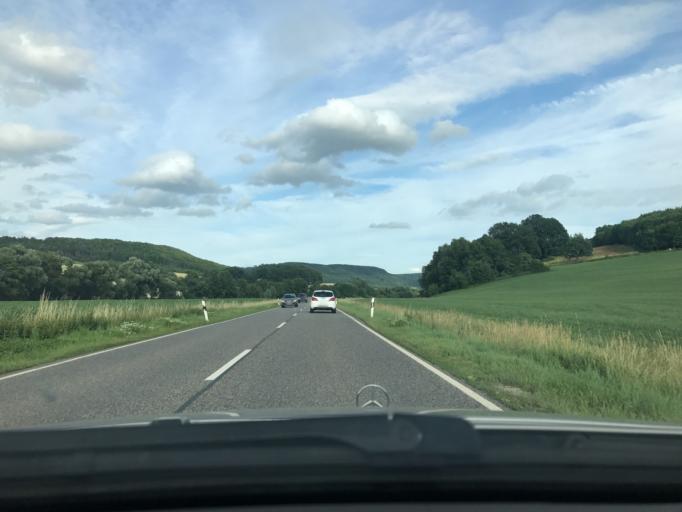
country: DE
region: Thuringia
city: Burgwalde
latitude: 51.3693
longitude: 10.0514
